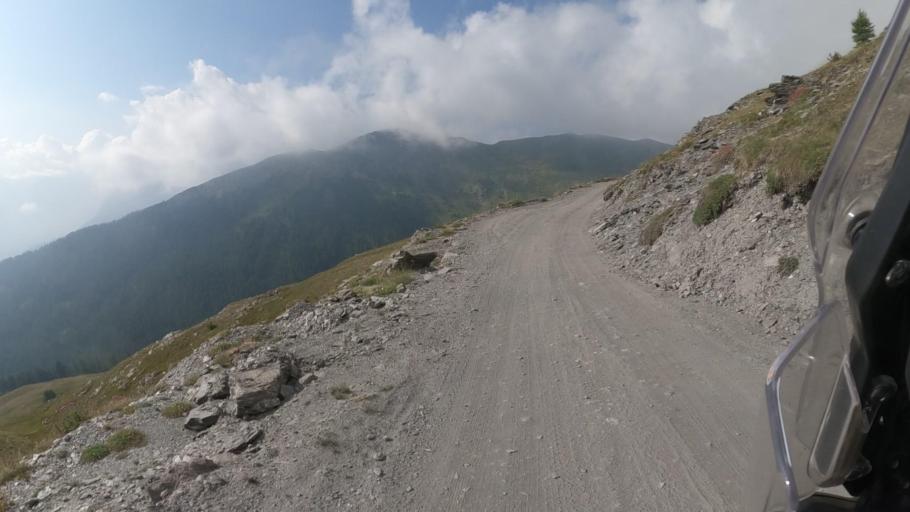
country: IT
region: Piedmont
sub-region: Provincia di Torino
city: Sauze d'Oulx
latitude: 44.9981
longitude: 6.8828
